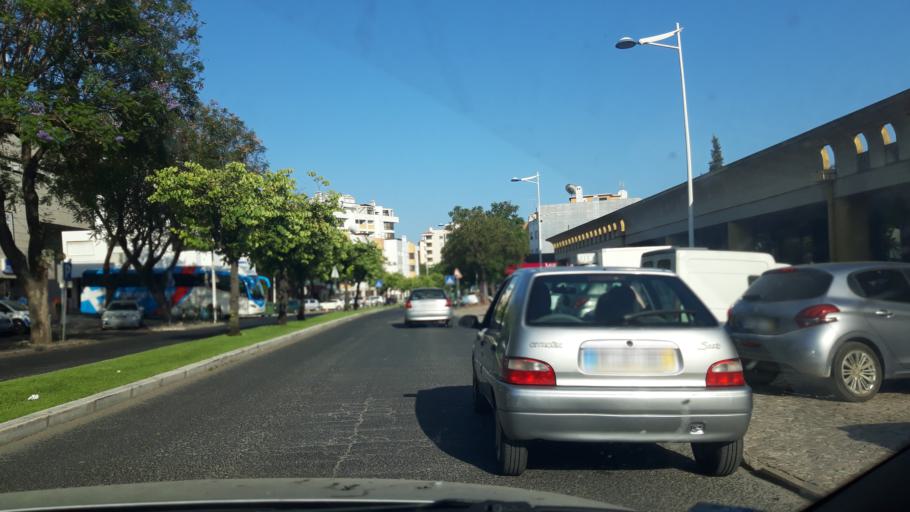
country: PT
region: Santarem
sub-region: Torres Novas
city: Torres Novas
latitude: 39.4773
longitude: -8.5372
